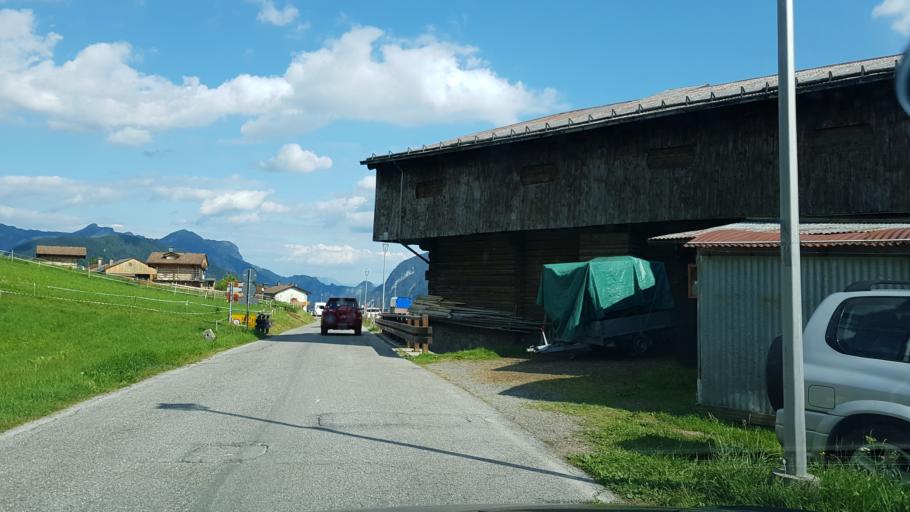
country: IT
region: Friuli Venezia Giulia
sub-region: Provincia di Udine
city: Sauris di Sotto
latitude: 46.4683
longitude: 12.6796
